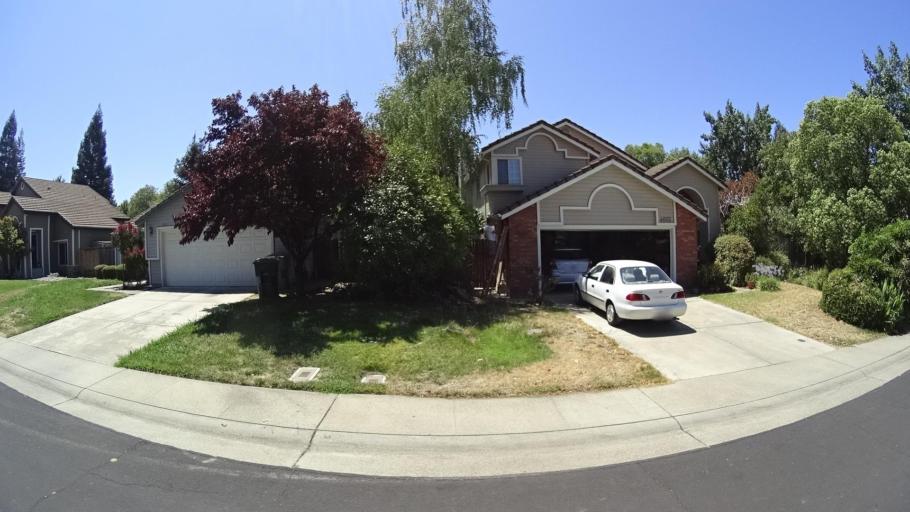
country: US
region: California
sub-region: Placer County
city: Rocklin
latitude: 38.8257
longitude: -121.2515
